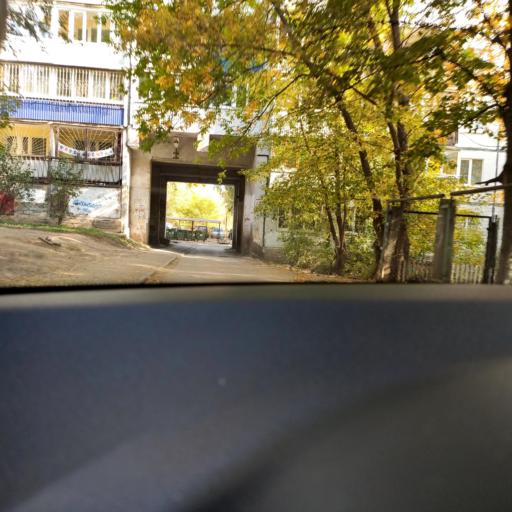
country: RU
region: Samara
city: Samara
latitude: 53.2434
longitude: 50.2597
